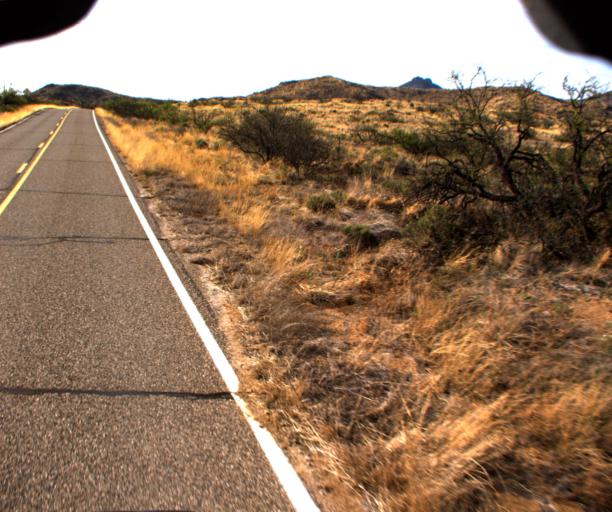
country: US
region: Arizona
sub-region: Cochise County
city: Willcox
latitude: 32.1622
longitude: -109.5735
